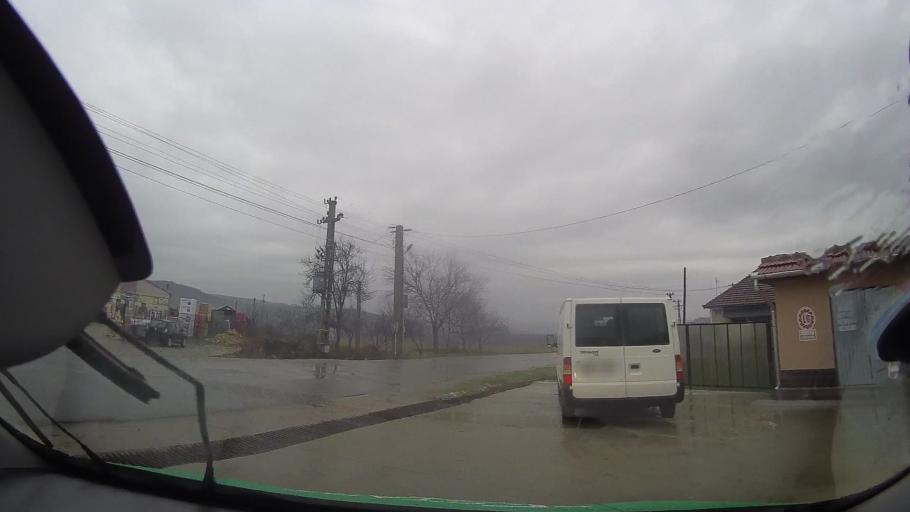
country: RO
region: Bihor
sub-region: Comuna Rabagani
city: Rabagani
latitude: 46.7483
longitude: 22.2369
